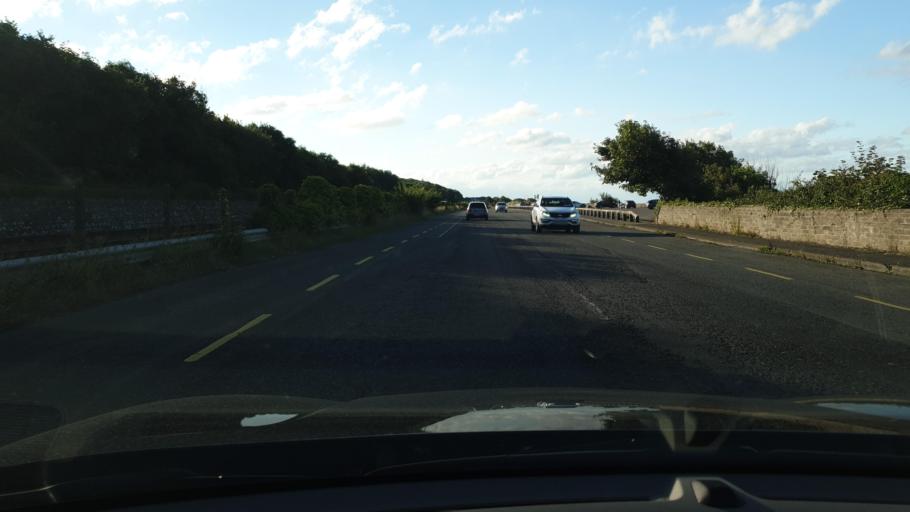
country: IE
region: Leinster
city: Balrothery
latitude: 53.5874
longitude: -6.1519
